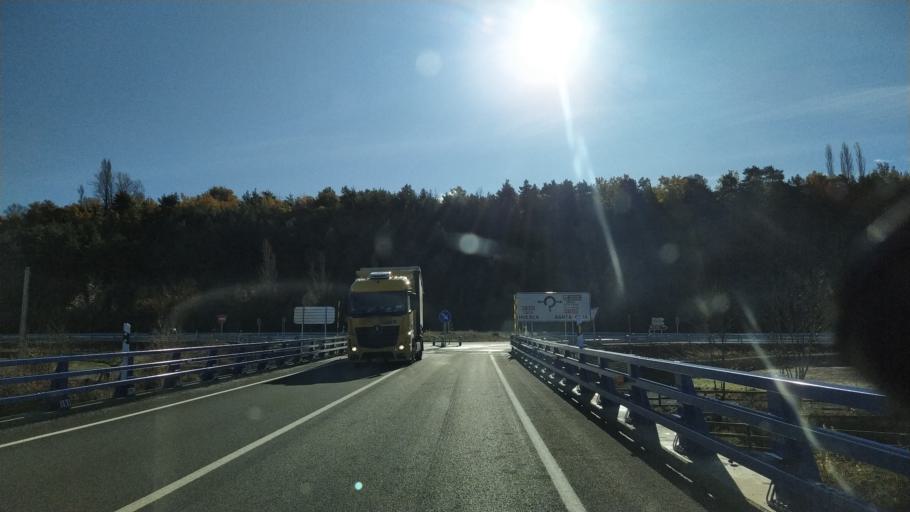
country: ES
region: Aragon
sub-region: Provincia de Huesca
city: Jaca
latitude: 42.5601
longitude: -0.5929
